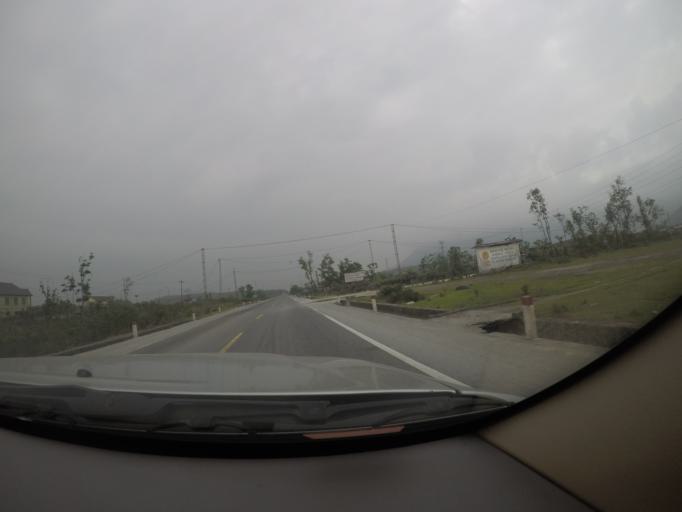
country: VN
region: Ha Tinh
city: Ky Anh
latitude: 18.0022
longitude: 106.4387
